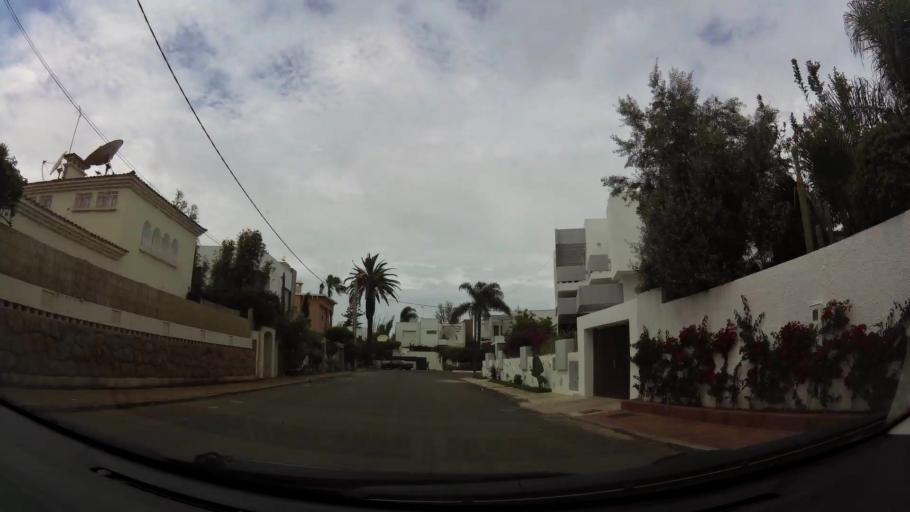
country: MA
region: Grand Casablanca
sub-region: Casablanca
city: Casablanca
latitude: 33.5736
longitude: -7.6606
